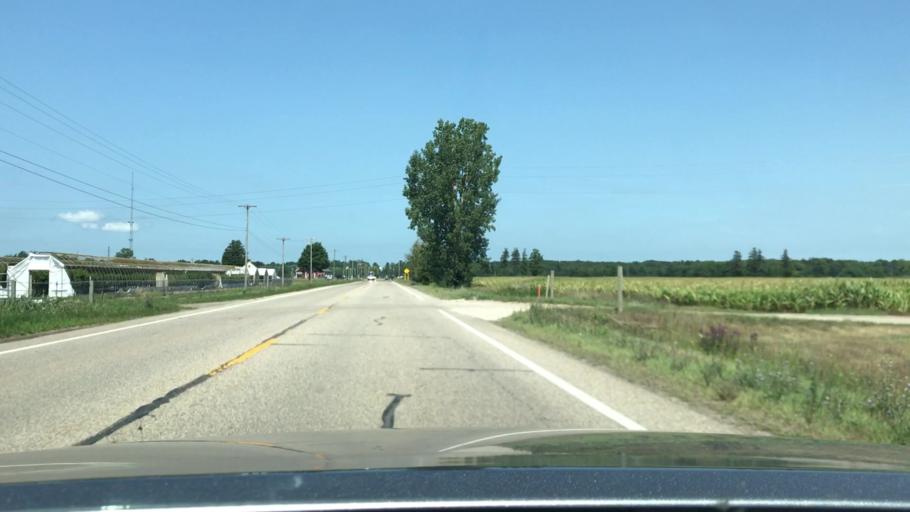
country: US
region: Michigan
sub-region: Ottawa County
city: Allendale
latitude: 42.9683
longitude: -86.0829
